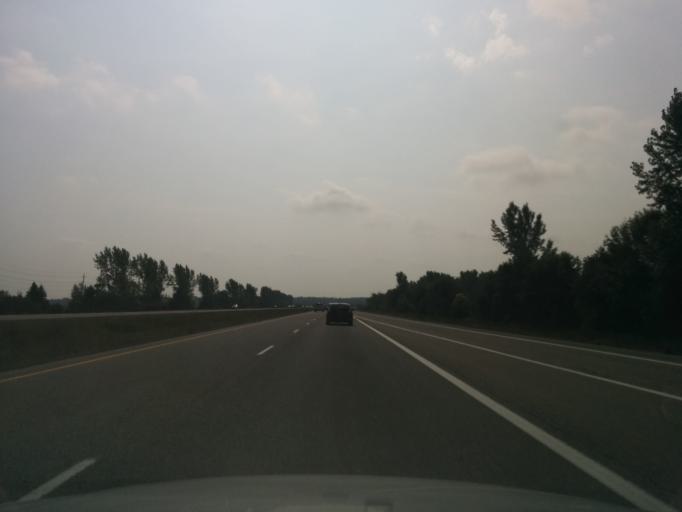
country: CA
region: Ontario
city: Bells Corners
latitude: 45.3092
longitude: -75.7988
